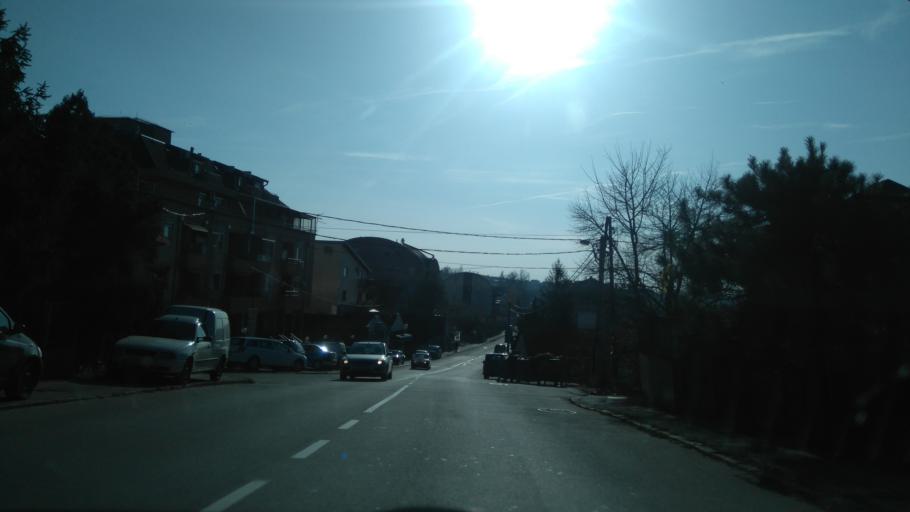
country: RS
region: Central Serbia
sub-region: Belgrade
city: Cukarica
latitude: 44.7585
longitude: 20.4059
